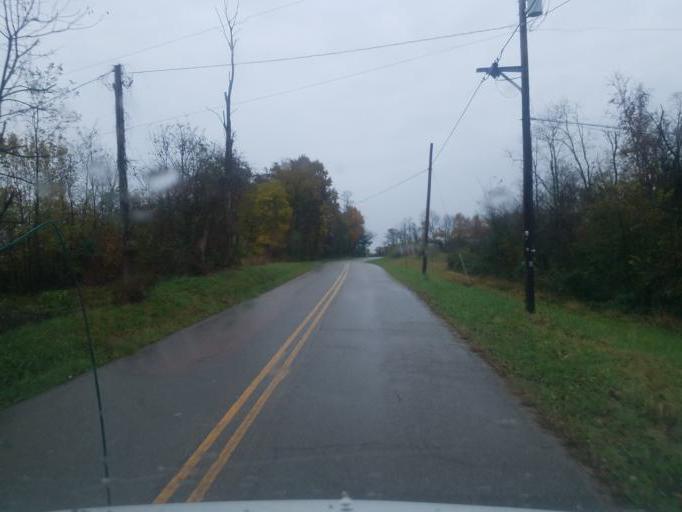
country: US
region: Ohio
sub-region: Washington County
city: Beverly
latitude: 39.4522
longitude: -81.6175
